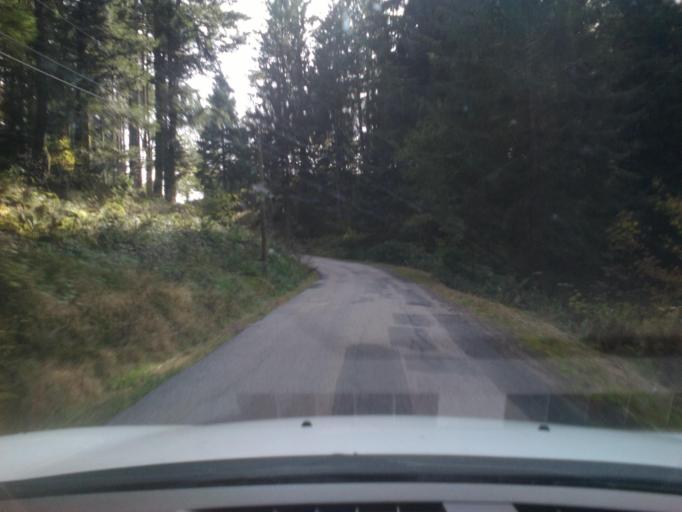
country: FR
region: Lorraine
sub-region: Departement des Vosges
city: Gerardmer
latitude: 48.0495
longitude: 6.8750
